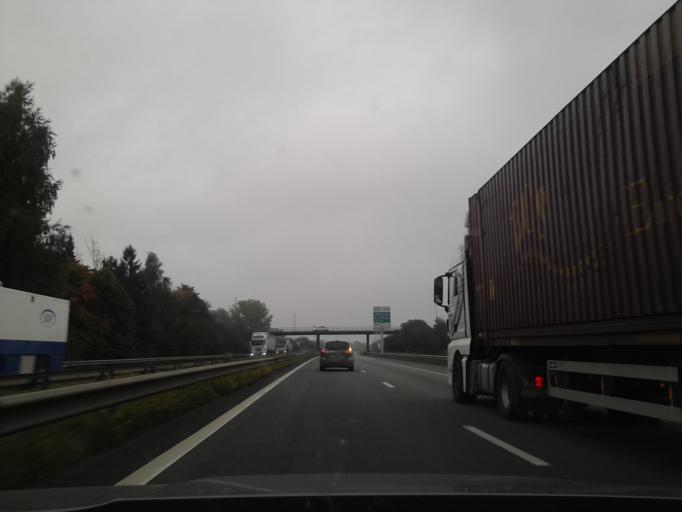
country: FR
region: Nord-Pas-de-Calais
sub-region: Departement du Nord
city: Lieu-Saint-Amand
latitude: 50.2656
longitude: 3.3318
